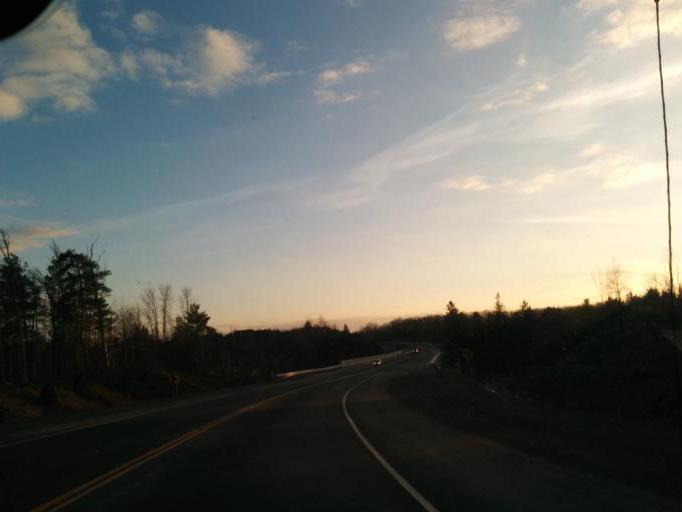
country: CA
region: Ontario
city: Brampton
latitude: 43.8860
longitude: -79.7714
